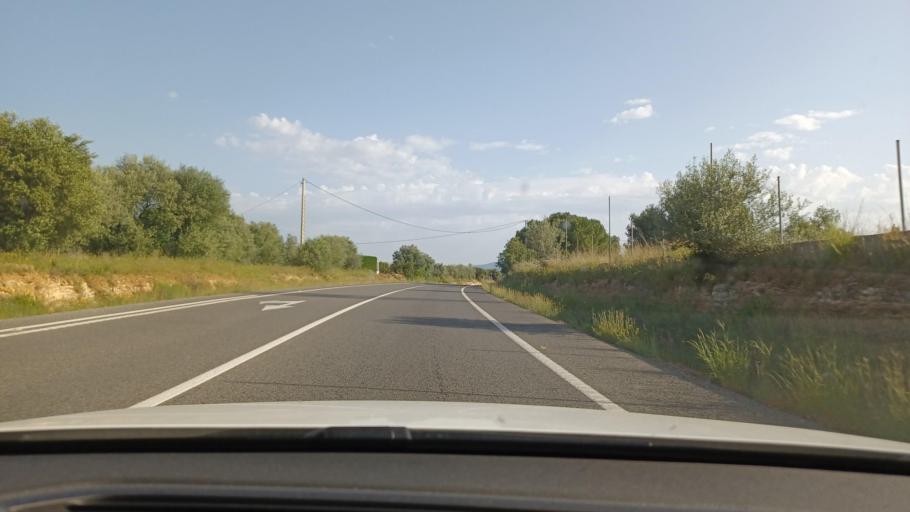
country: ES
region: Catalonia
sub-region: Provincia de Tarragona
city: Amposta
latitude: 40.7169
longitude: 0.5632
